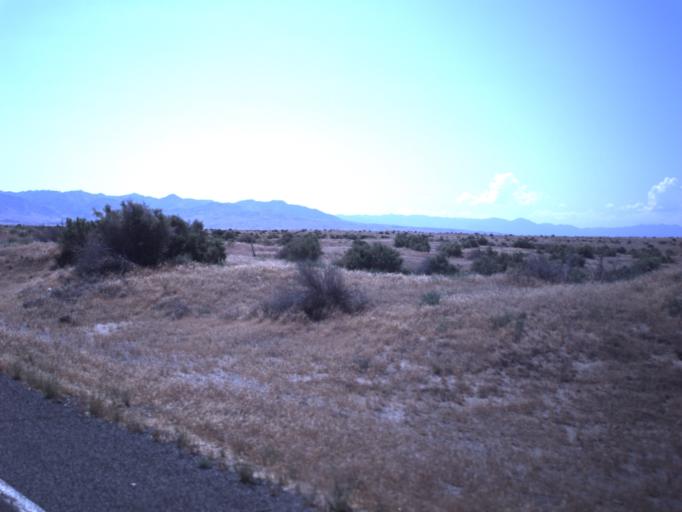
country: US
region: Utah
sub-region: Millard County
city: Delta
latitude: 39.4788
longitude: -112.5018
